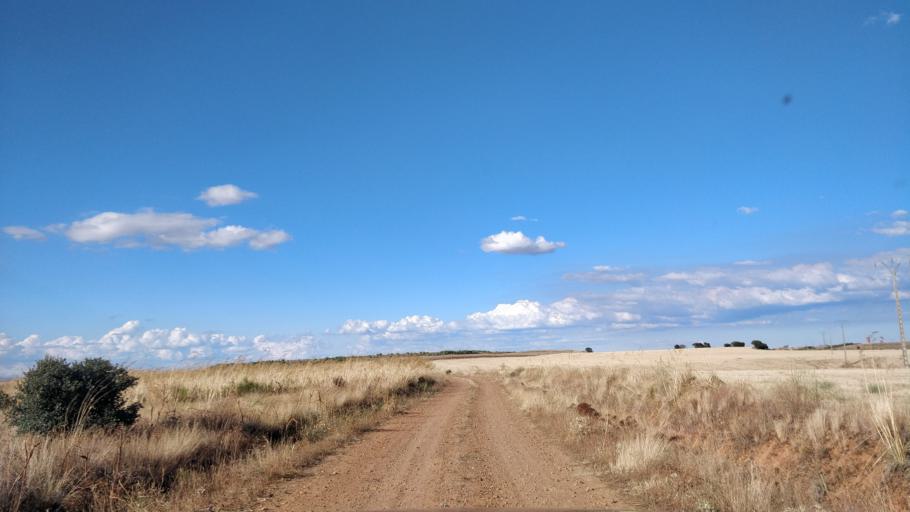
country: ES
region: Castille and Leon
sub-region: Provincia de Leon
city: Santa Cristina de Valmadrigal
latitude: 42.3404
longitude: -5.2724
